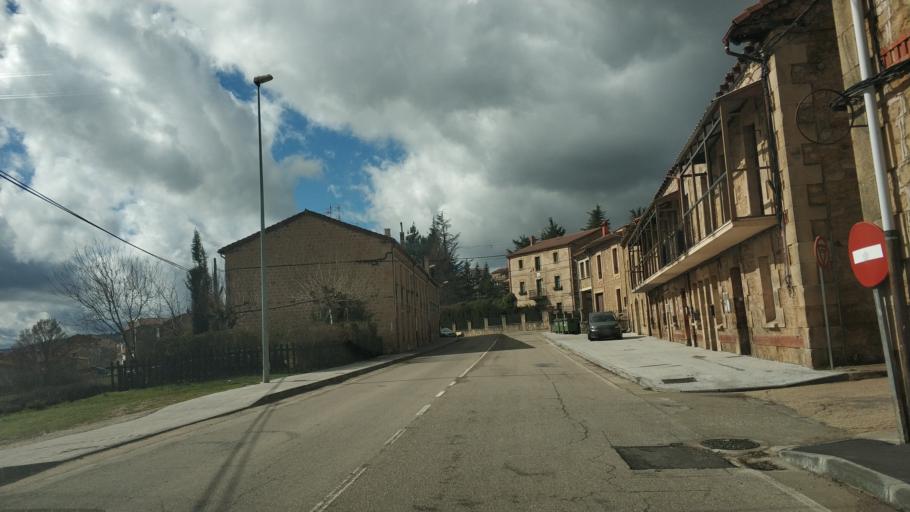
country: ES
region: Castille and Leon
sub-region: Provincia de Burgos
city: Quintanar de la Sierra
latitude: 41.9852
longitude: -3.0319
